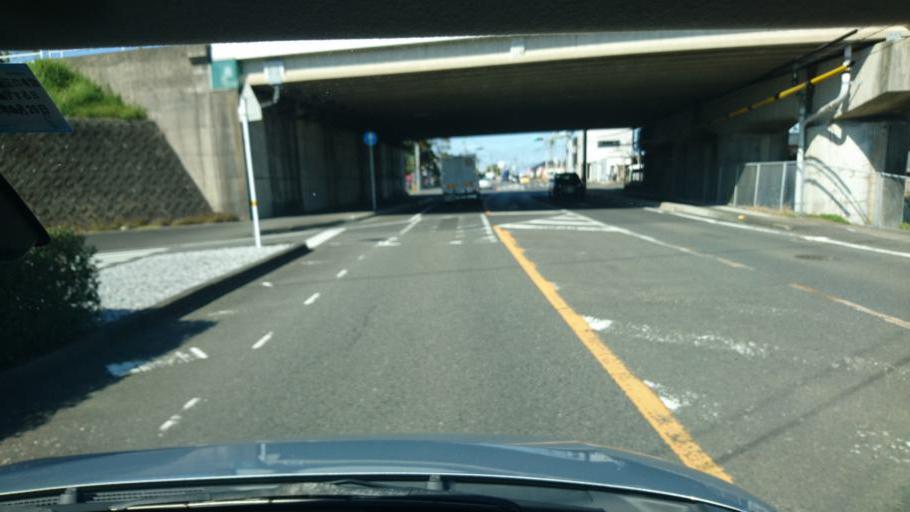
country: JP
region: Miyazaki
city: Miyazaki-shi
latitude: 31.8670
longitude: 131.4318
